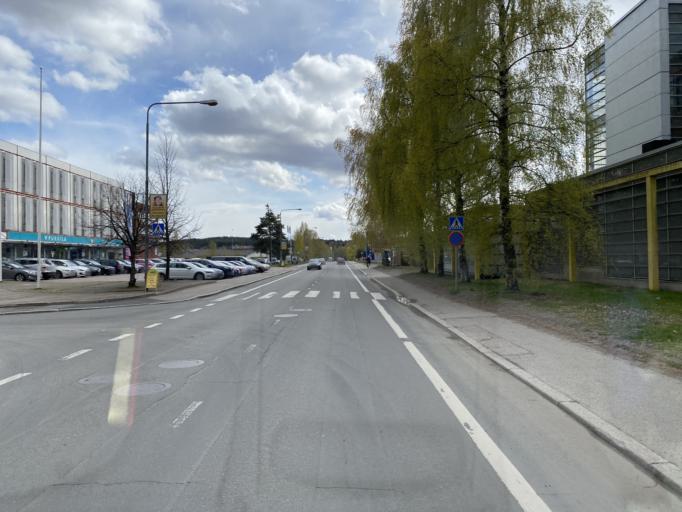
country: FI
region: Pirkanmaa
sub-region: Tampere
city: Tampere
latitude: 61.4810
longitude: 23.7826
